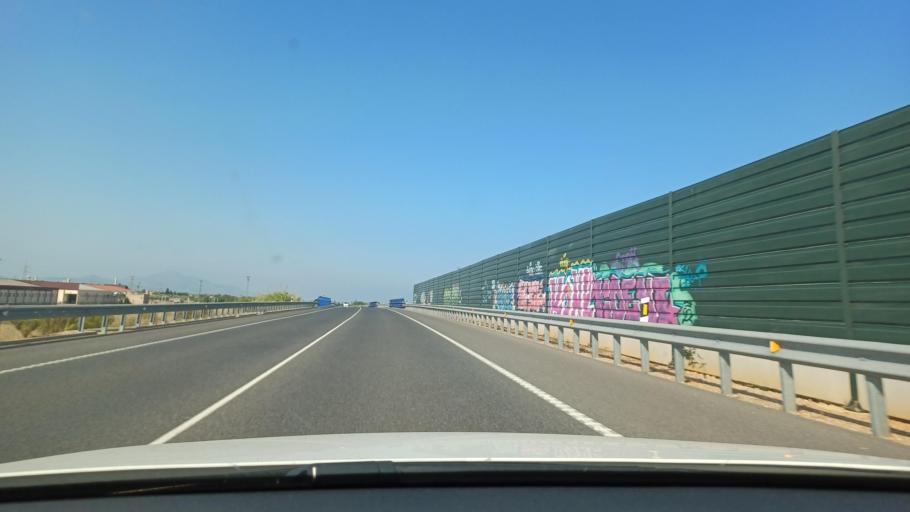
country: ES
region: Valencia
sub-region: Provincia de Castello
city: Benicarlo
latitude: 40.4307
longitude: 0.4042
